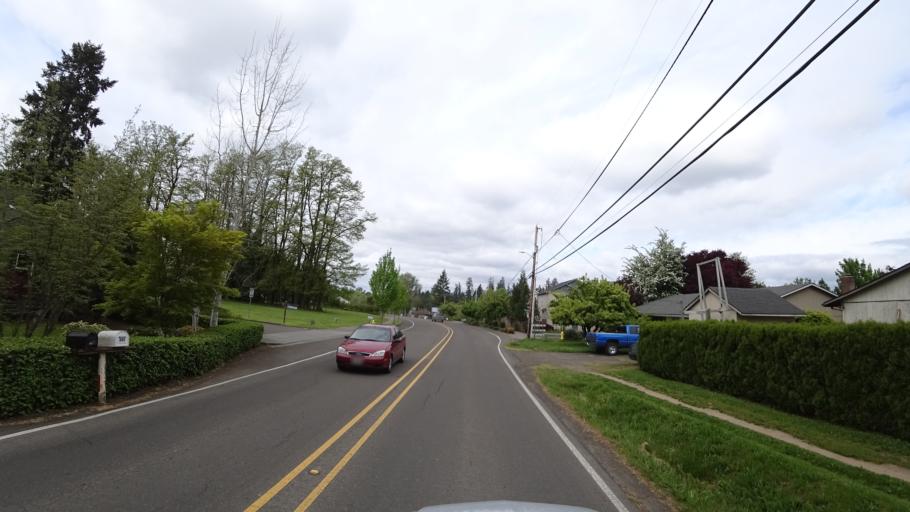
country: US
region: Oregon
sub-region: Washington County
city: Hillsboro
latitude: 45.5228
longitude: -122.9995
